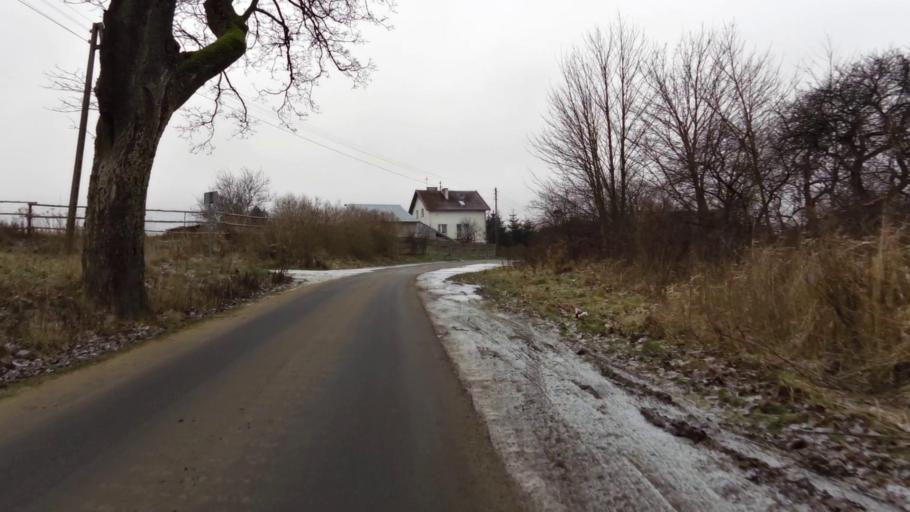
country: PL
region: West Pomeranian Voivodeship
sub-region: Powiat szczecinecki
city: Szczecinek
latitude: 53.6523
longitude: 16.6342
